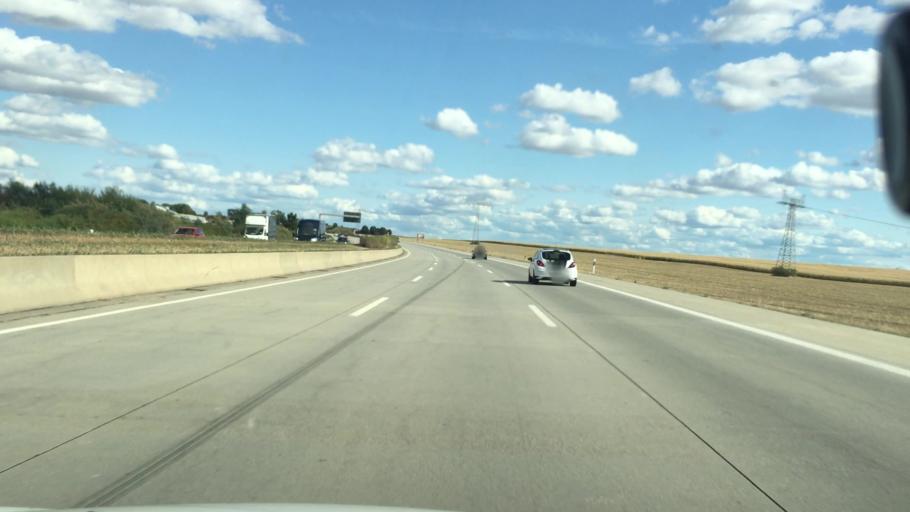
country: DE
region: Thuringia
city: Schwaara
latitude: 50.8797
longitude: 12.1597
